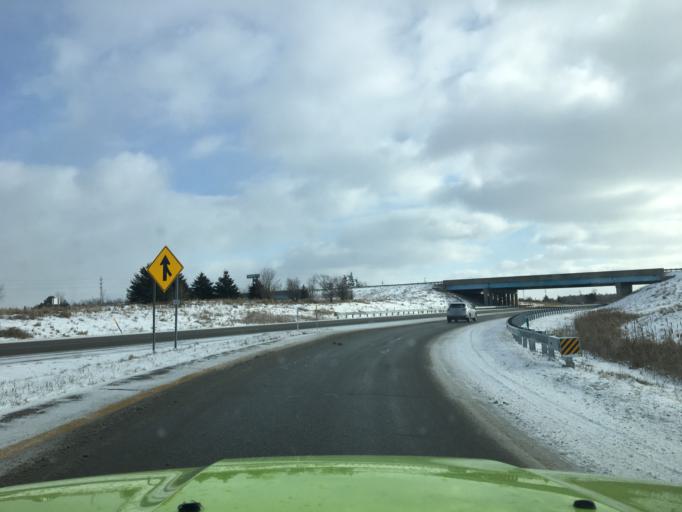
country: US
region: Michigan
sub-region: Mecosta County
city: Big Rapids
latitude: 43.6880
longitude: -85.5223
